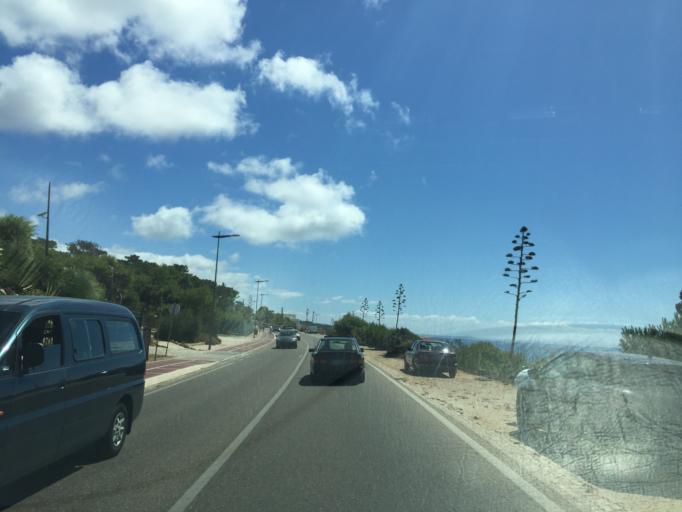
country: PT
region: Lisbon
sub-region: Cascais
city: Cascais
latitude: 38.6956
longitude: -9.4590
